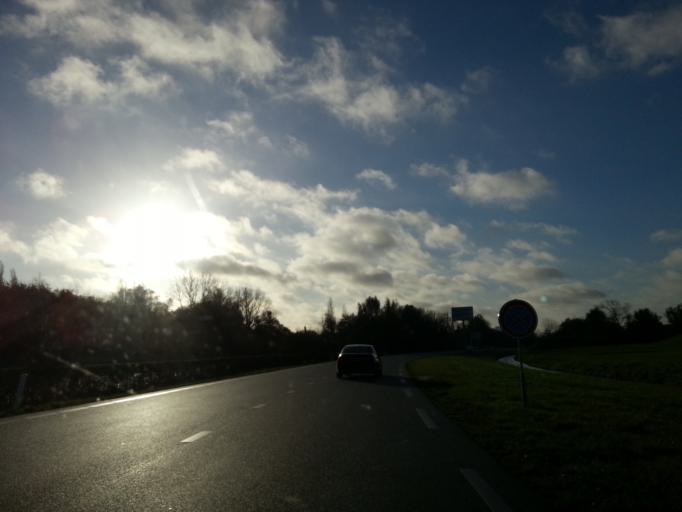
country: NL
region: South Holland
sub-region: Gemeente Lansingerland
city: Berkel en Rodenrijs
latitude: 51.9639
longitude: 4.4609
